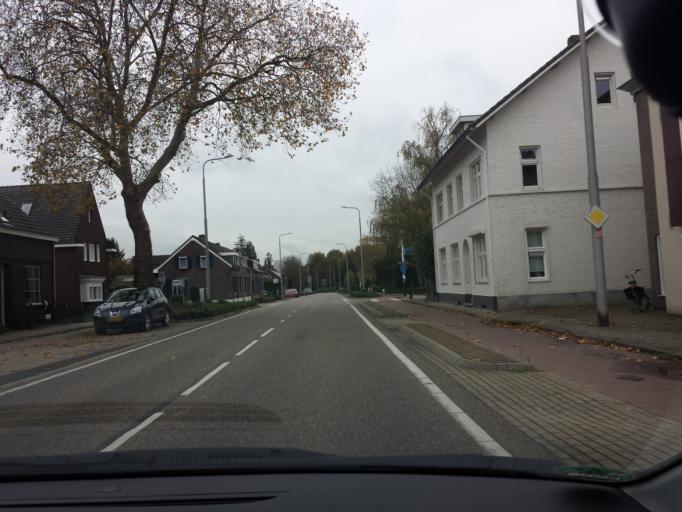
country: NL
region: Limburg
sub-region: Gemeente Venlo
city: Tegelen
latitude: 51.3308
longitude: 6.1250
